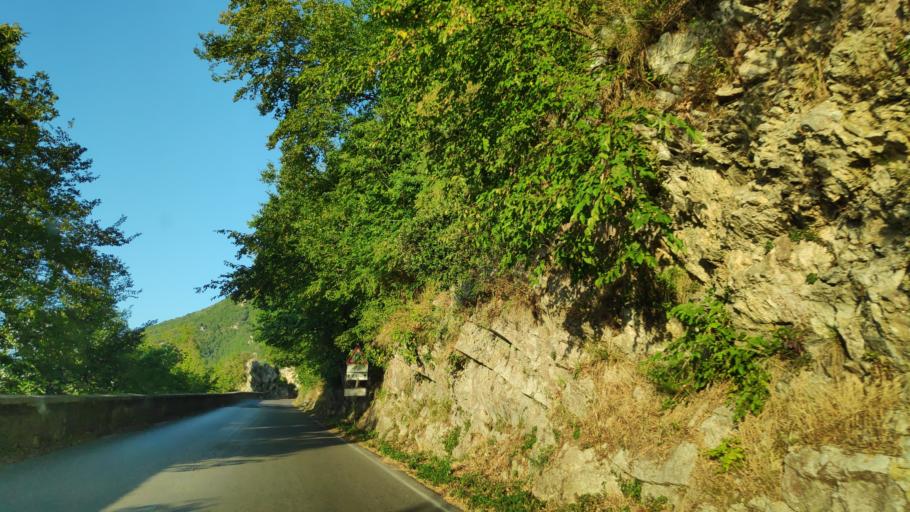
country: IT
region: Campania
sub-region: Provincia di Salerno
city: Corbara
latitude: 40.7189
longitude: 14.6086
